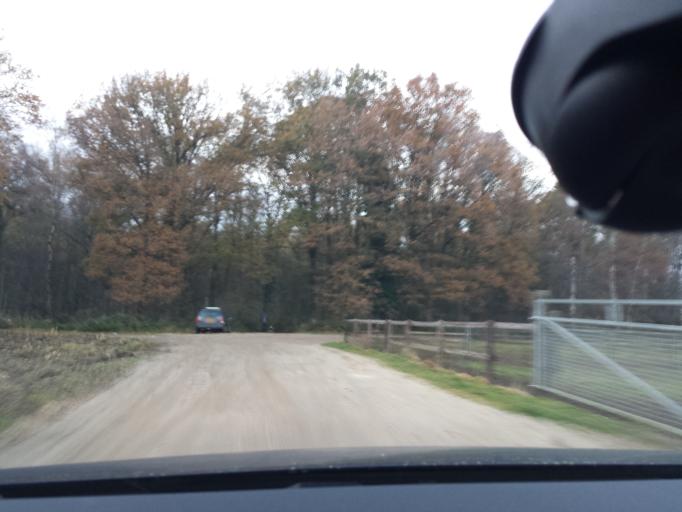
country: NL
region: Limburg
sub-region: Gemeente Heerlen
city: Heerlen
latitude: 50.9226
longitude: 6.0236
